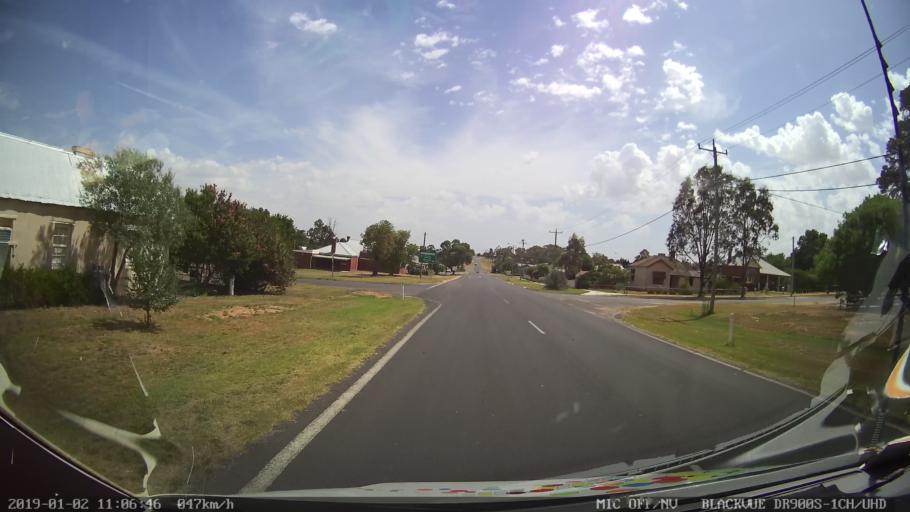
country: AU
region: New South Wales
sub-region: Young
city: Young
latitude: -34.5533
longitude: 148.3573
